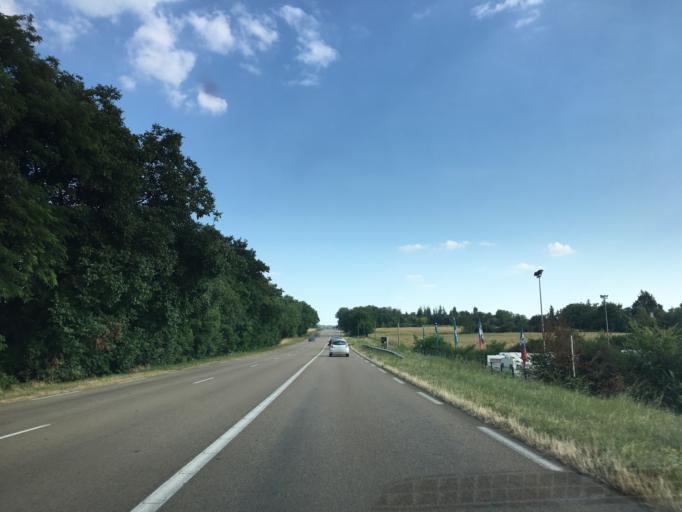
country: FR
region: Bourgogne
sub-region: Departement de l'Yonne
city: Maillot
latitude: 48.1626
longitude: 3.3015
